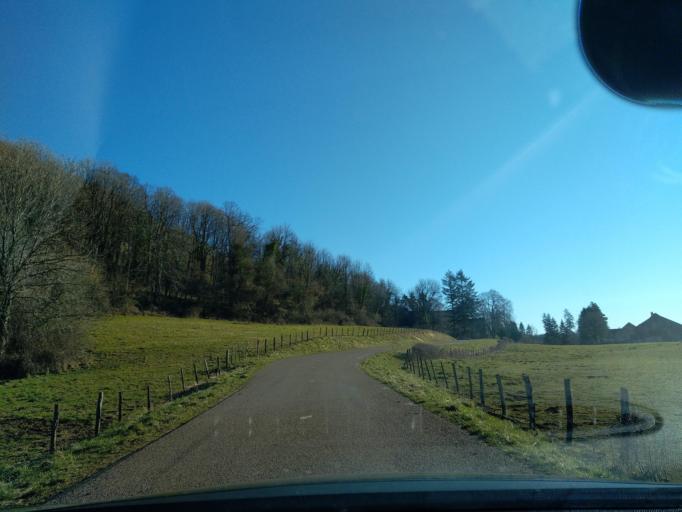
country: FR
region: Franche-Comte
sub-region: Departement du Jura
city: Clairvaux-les-Lacs
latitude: 46.7031
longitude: 5.7329
